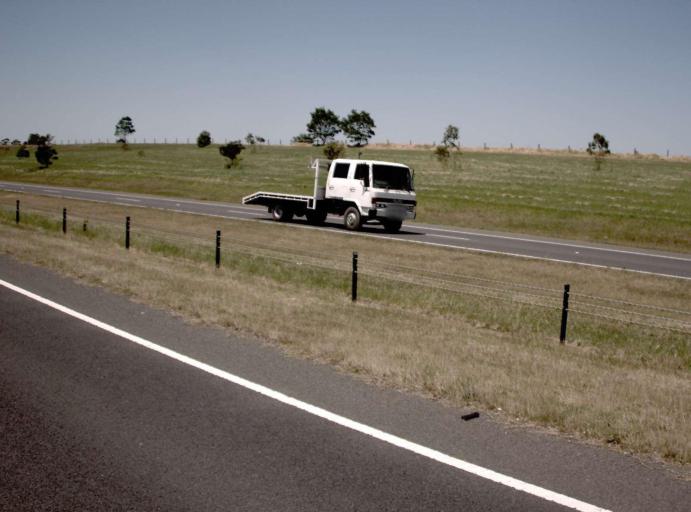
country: AU
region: Victoria
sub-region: Cardinia
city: Officer South
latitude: -38.0652
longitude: 145.3749
